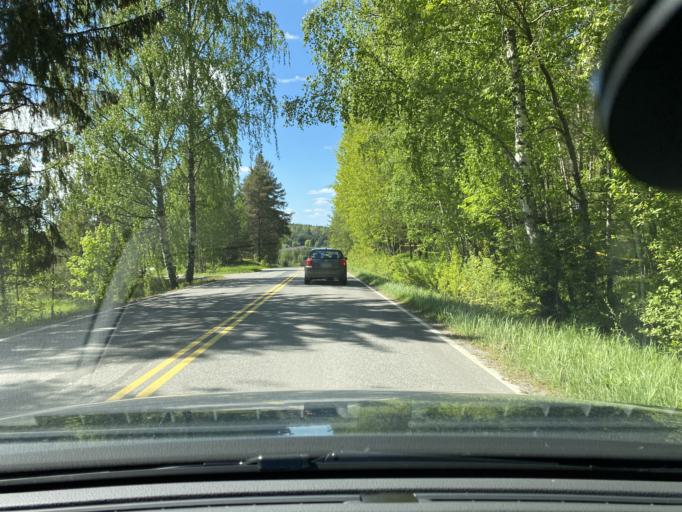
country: FI
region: Varsinais-Suomi
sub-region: Salo
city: Halikko
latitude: 60.3682
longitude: 23.0076
